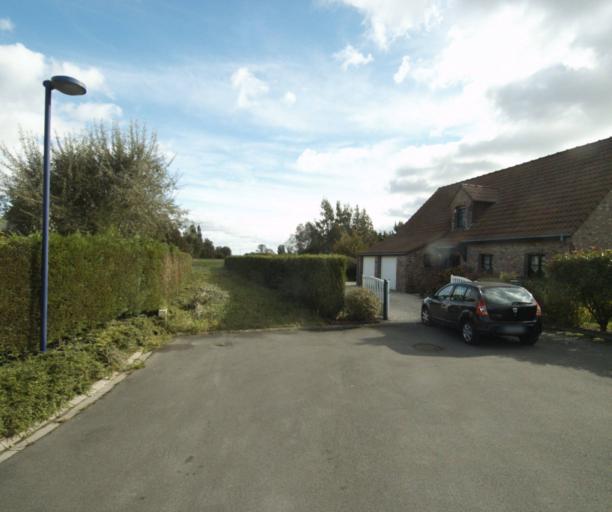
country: FR
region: Nord-Pas-de-Calais
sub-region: Departement du Nord
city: Armentieres
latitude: 50.6682
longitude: 2.8950
